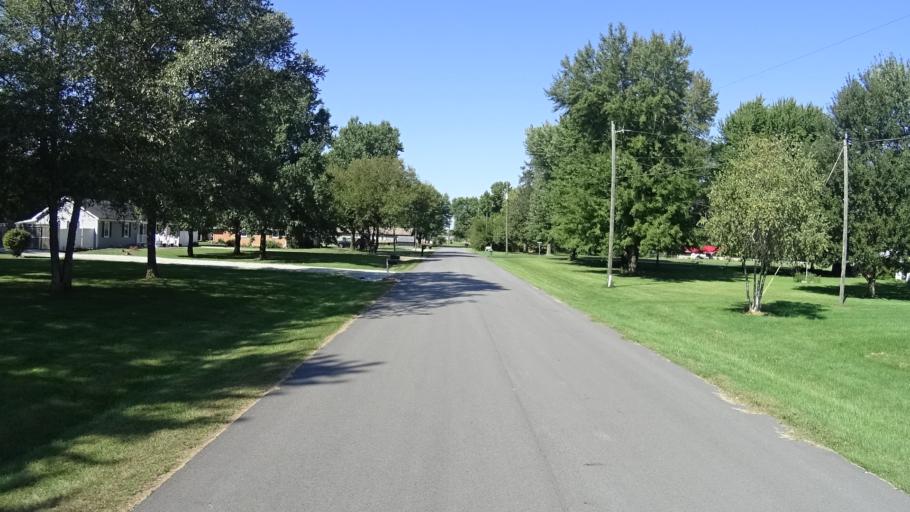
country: US
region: Indiana
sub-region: Madison County
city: Lapel
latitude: 40.0575
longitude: -85.8418
